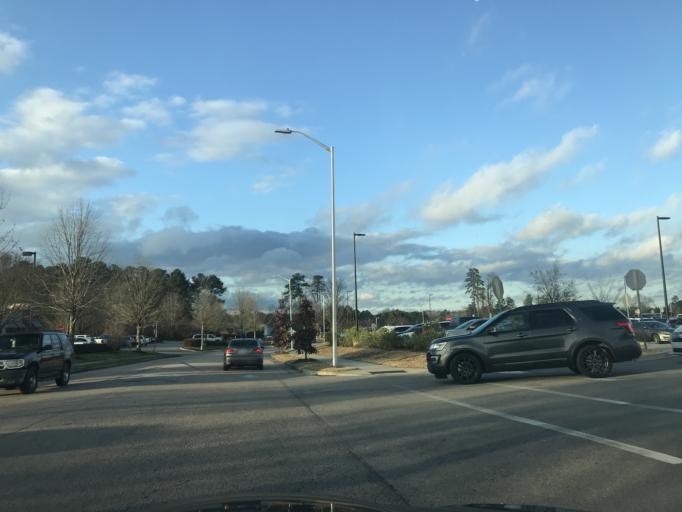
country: US
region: North Carolina
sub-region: Wake County
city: Wake Forest
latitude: 35.9562
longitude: -78.5396
